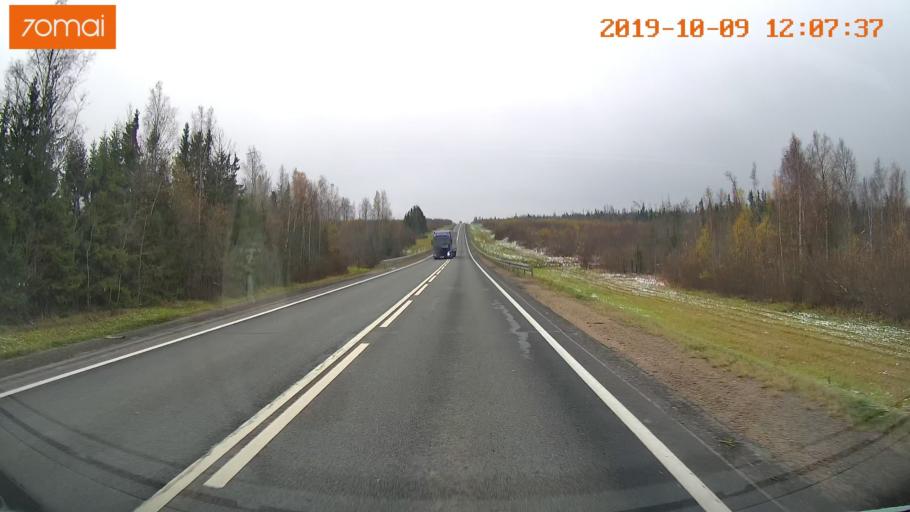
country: RU
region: Jaroslavl
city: Prechistoye
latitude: 58.5970
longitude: 40.3430
